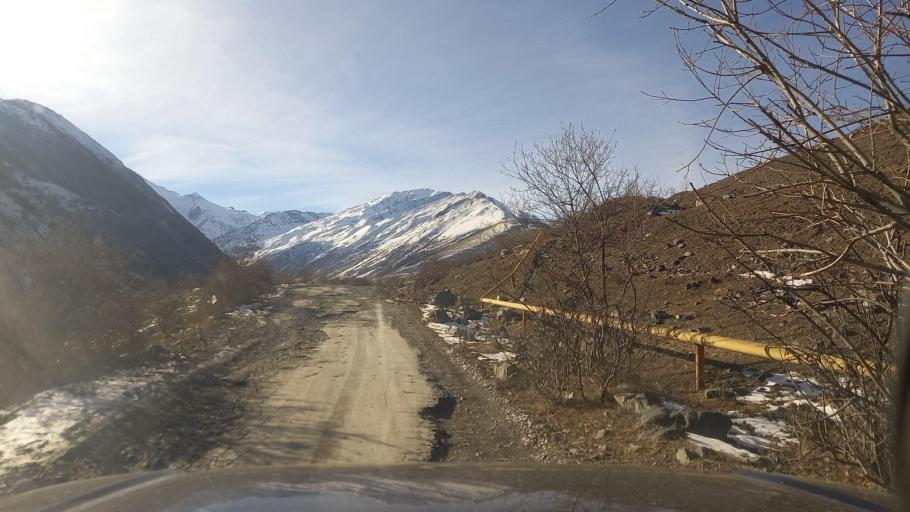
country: RU
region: Ingushetiya
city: Dzhayrakh
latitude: 42.8403
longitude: 44.5130
